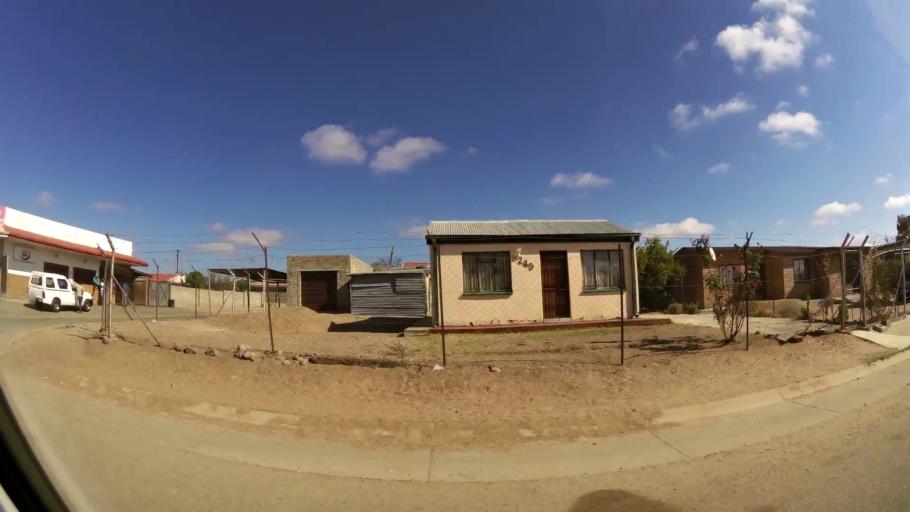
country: ZA
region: Limpopo
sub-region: Capricorn District Municipality
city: Polokwane
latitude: -23.8660
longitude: 29.3940
